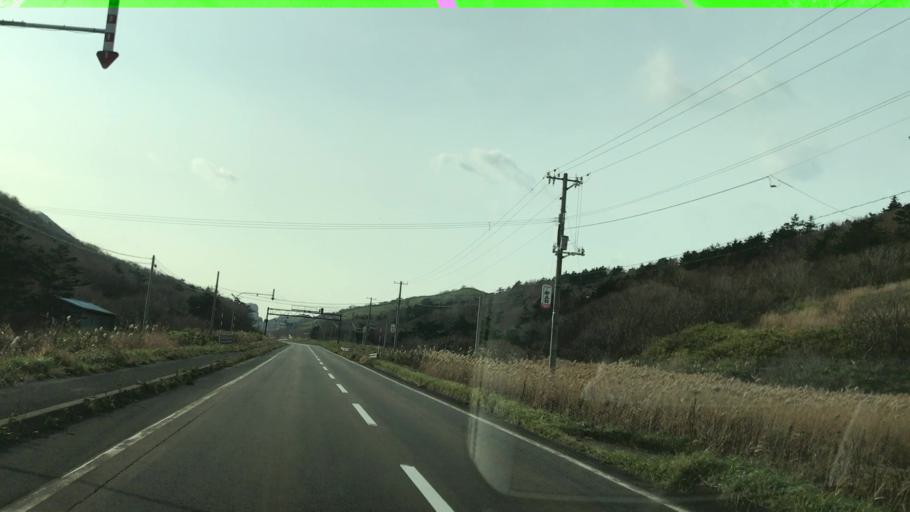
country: JP
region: Hokkaido
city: Iwanai
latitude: 43.3271
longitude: 140.3649
